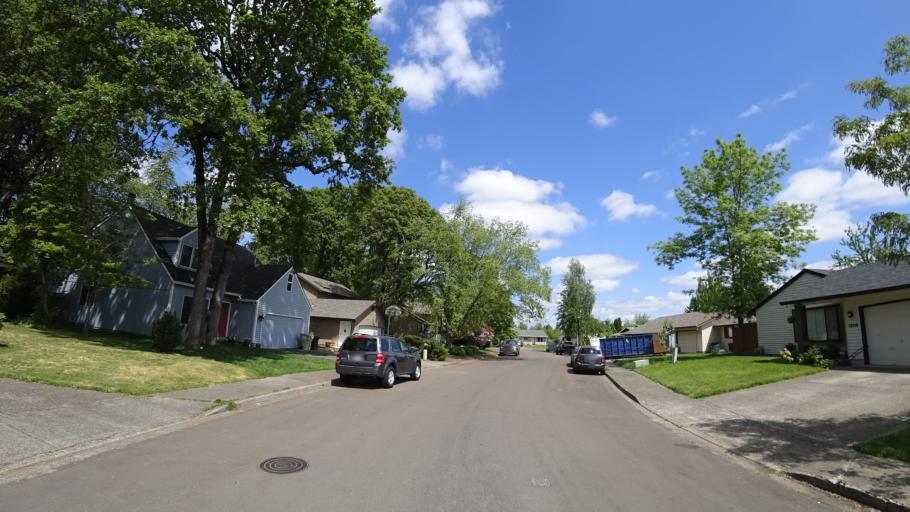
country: US
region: Oregon
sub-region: Washington County
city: Aloha
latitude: 45.5104
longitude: -122.8941
